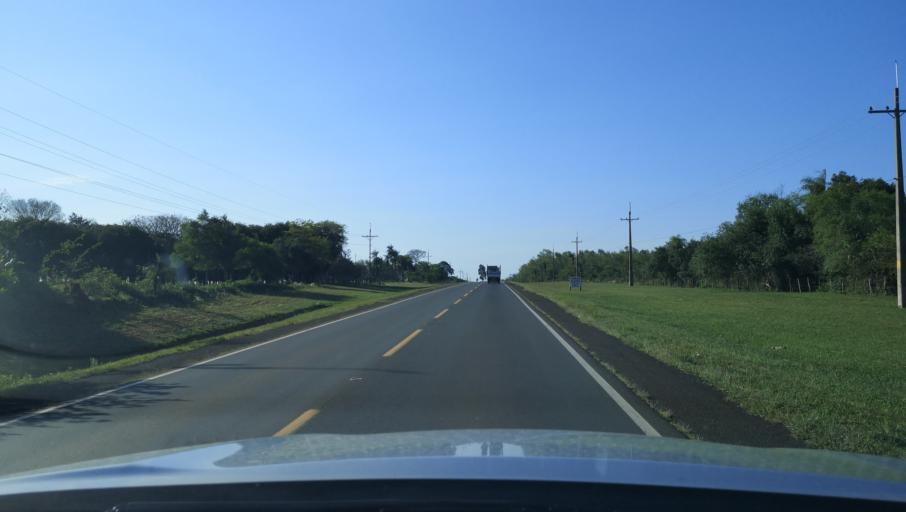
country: PY
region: Misiones
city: Santa Maria
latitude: -26.7688
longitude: -57.0313
